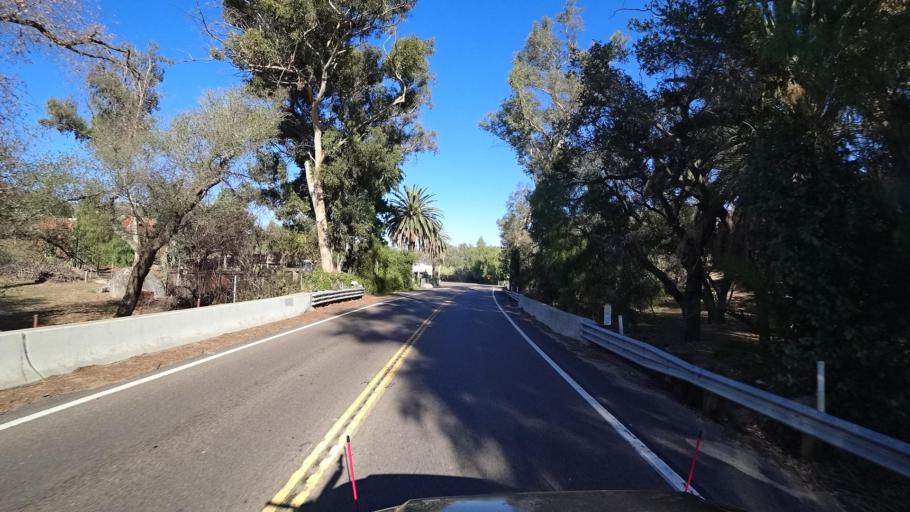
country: US
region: California
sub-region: San Diego County
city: Jamul
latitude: 32.6431
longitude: -116.7799
